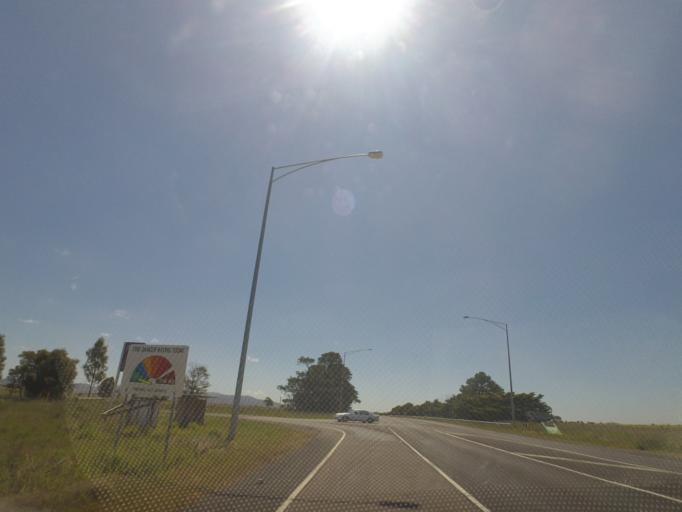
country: AU
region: Victoria
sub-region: Hume
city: Sunbury
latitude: -37.4826
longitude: 144.7526
